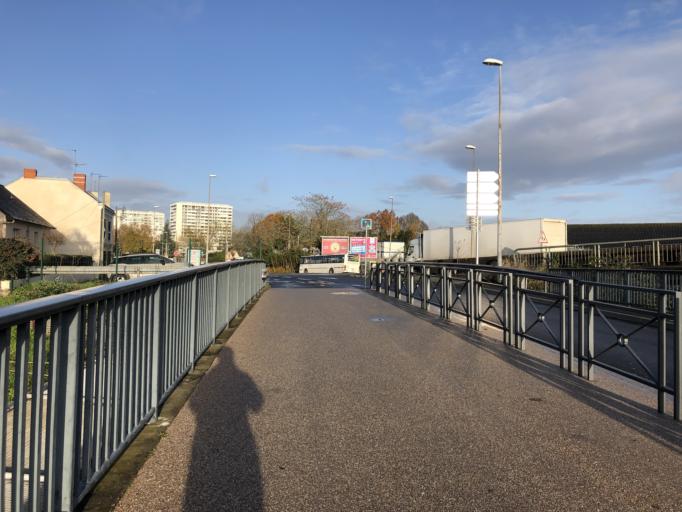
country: FR
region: Pays de la Loire
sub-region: Departement de Maine-et-Loire
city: Angers
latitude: 47.4678
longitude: -0.5300
